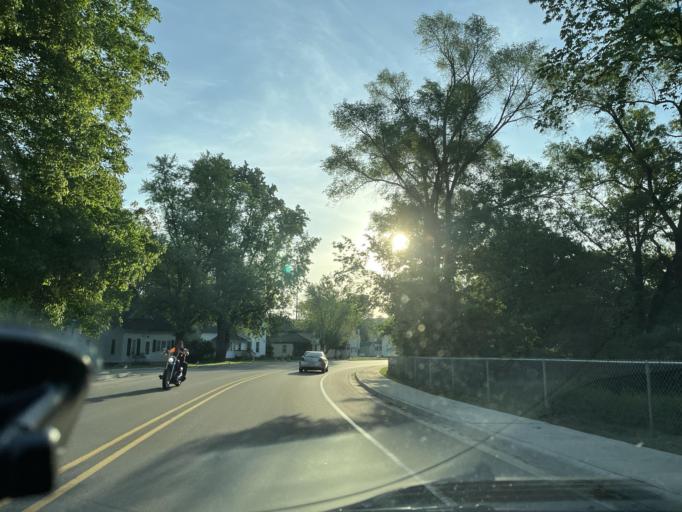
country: US
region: Michigan
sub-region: Barry County
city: Middleville
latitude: 42.7137
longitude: -85.4607
